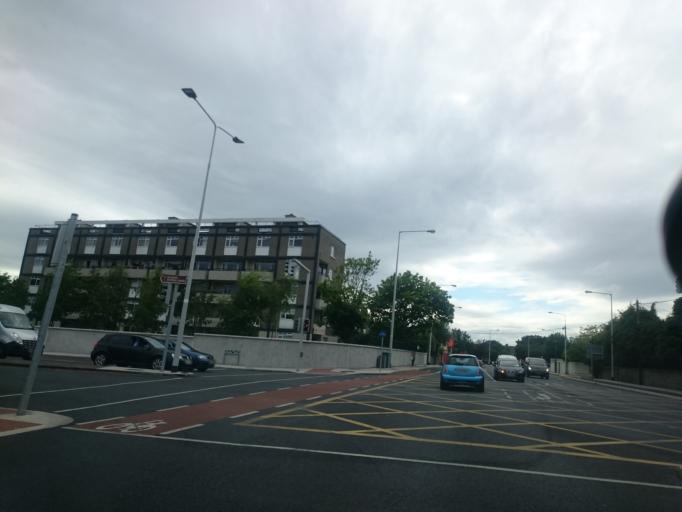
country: IE
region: Leinster
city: Dundrum
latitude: 53.2953
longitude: -6.2568
